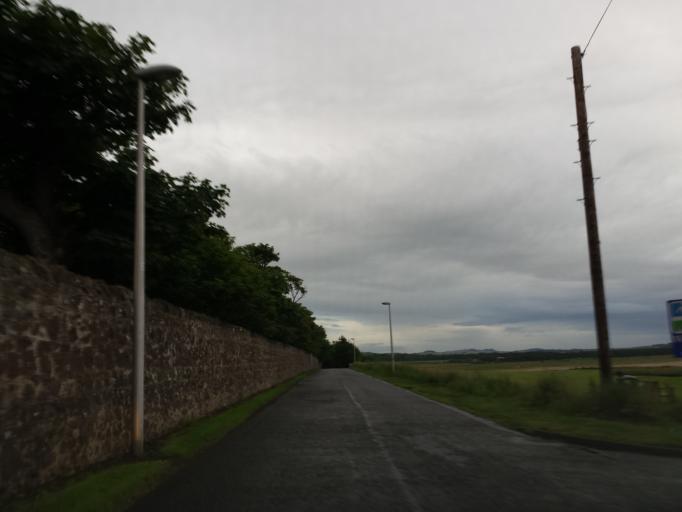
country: GB
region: Scotland
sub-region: East Lothian
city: Dunbar
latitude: 56.0015
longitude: -2.5366
